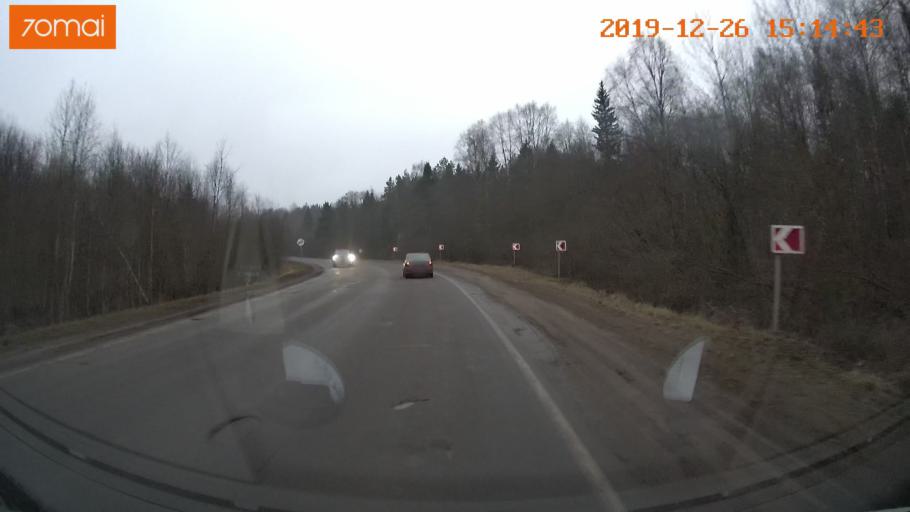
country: RU
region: Jaroslavl
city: Rybinsk
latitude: 58.1037
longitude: 38.8776
